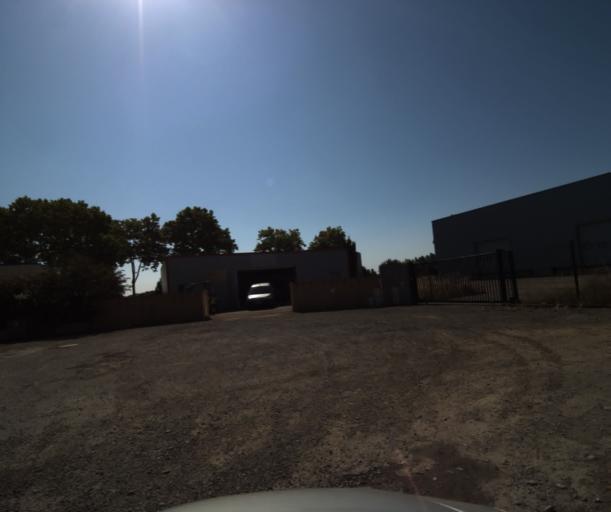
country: FR
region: Midi-Pyrenees
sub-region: Departement de la Haute-Garonne
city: Lagardelle-sur-Leze
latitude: 43.4176
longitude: 1.3730
